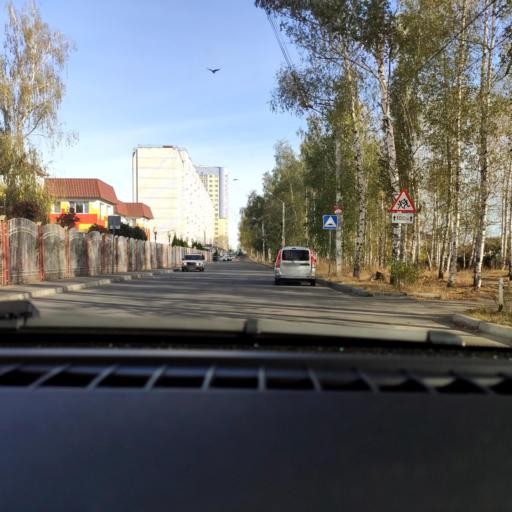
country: RU
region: Voronezj
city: Somovo
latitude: 51.7394
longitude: 39.3194
